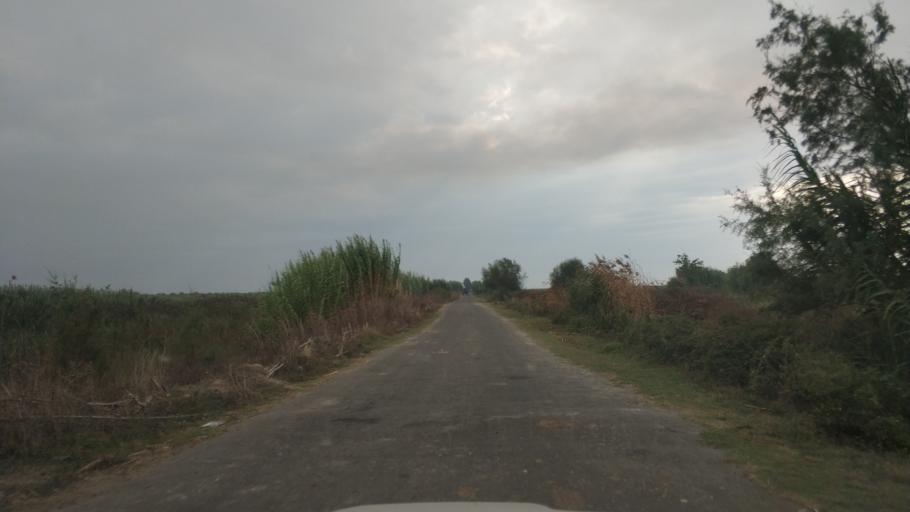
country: AL
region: Fier
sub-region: Rrethi i Fierit
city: Dermenas
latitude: 40.7277
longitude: 19.4632
